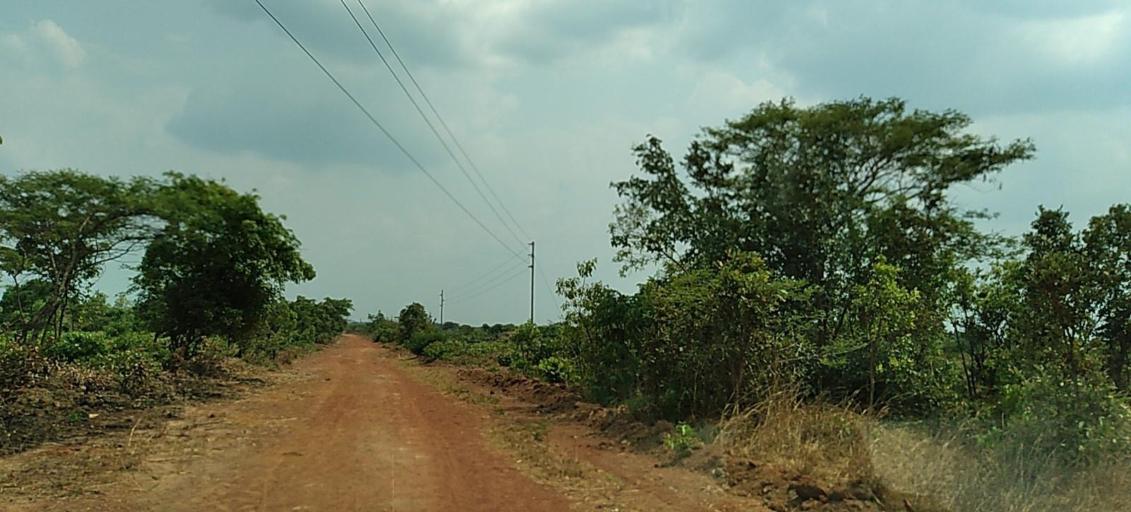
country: ZM
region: Copperbelt
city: Kalulushi
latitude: -12.8807
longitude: 28.0748
